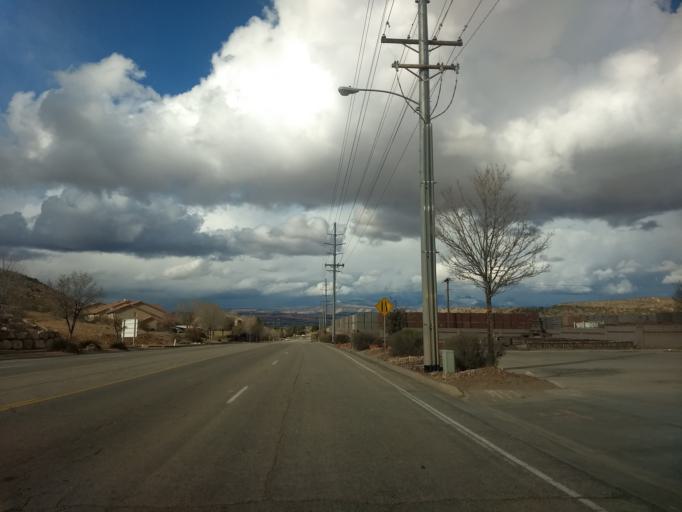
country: US
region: Utah
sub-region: Washington County
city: Saint George
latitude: 37.0463
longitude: -113.5551
